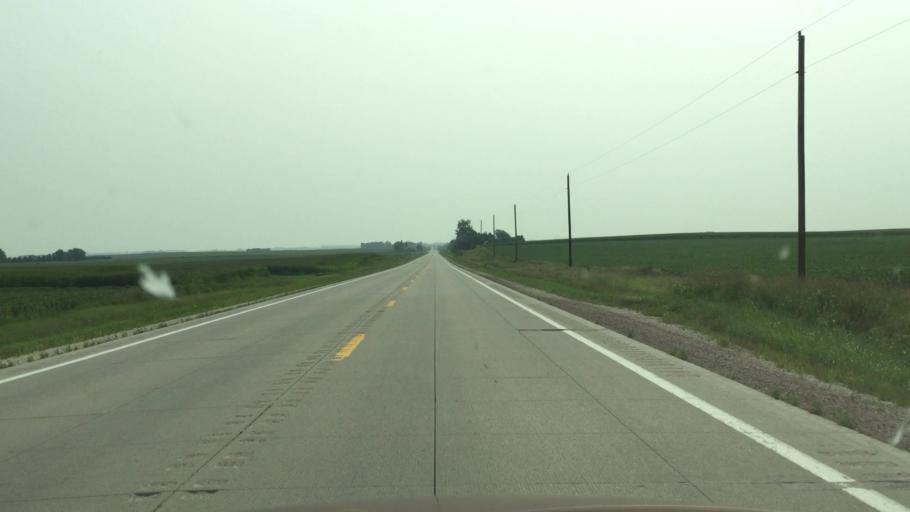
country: US
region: Iowa
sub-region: Osceola County
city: Sibley
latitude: 43.4327
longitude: -95.6571
